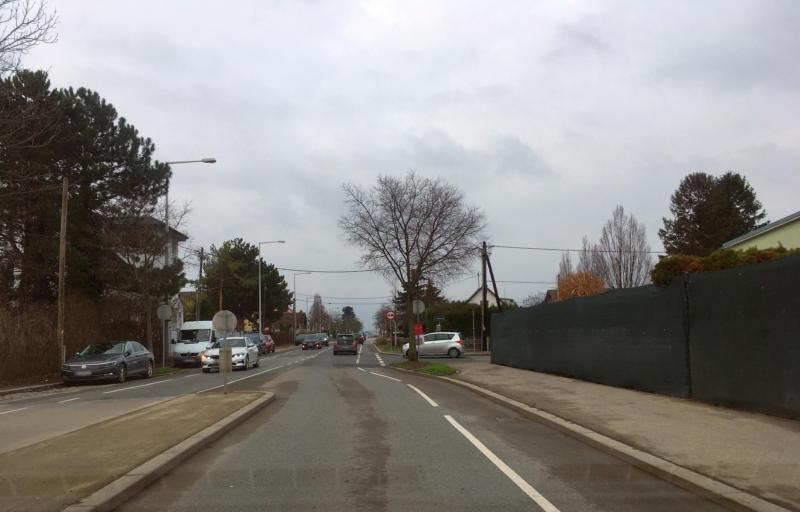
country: AT
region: Lower Austria
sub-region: Politischer Bezirk Wien-Umgebung
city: Gerasdorf bei Wien
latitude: 48.2559
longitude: 16.4908
